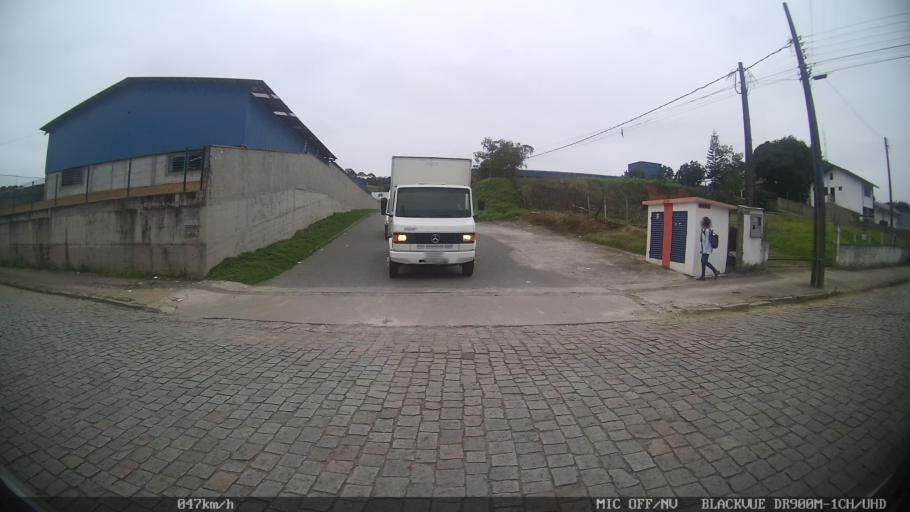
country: BR
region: Santa Catarina
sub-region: Joinville
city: Joinville
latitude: -26.3393
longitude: -48.8574
